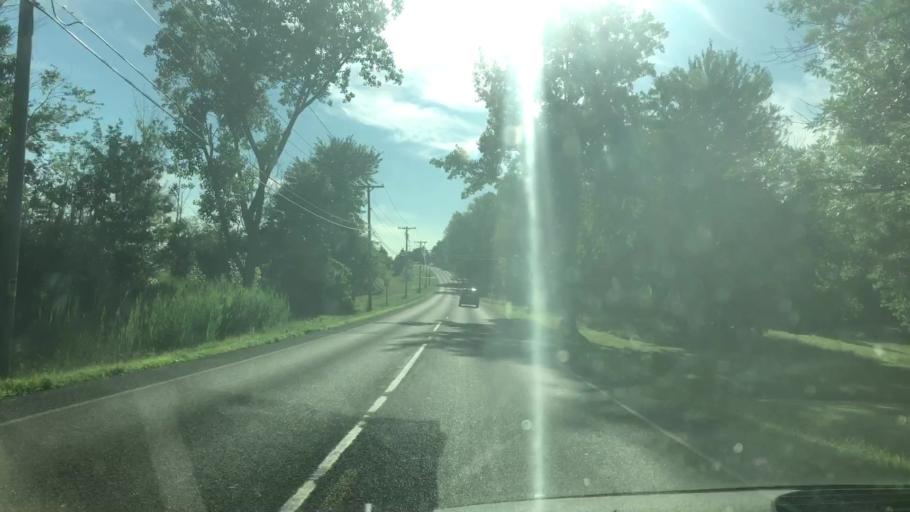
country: US
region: New York
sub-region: Wayne County
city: Macedon
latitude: 43.0442
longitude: -77.3530
